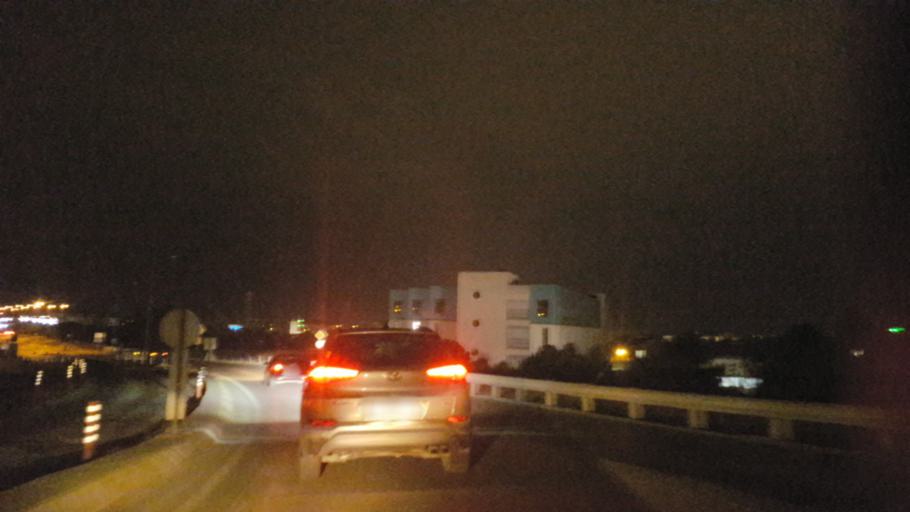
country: TR
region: Istanbul
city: Icmeler
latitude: 40.8338
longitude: 29.3257
